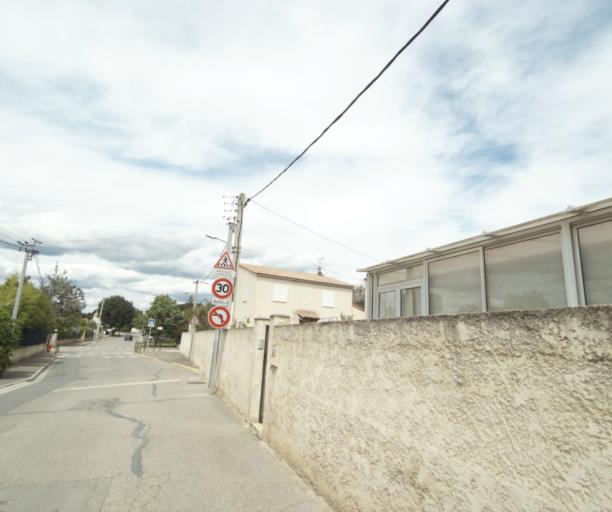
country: FR
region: Provence-Alpes-Cote d'Azur
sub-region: Departement des Bouches-du-Rhone
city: Rognac
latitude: 43.4847
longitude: 5.2368
